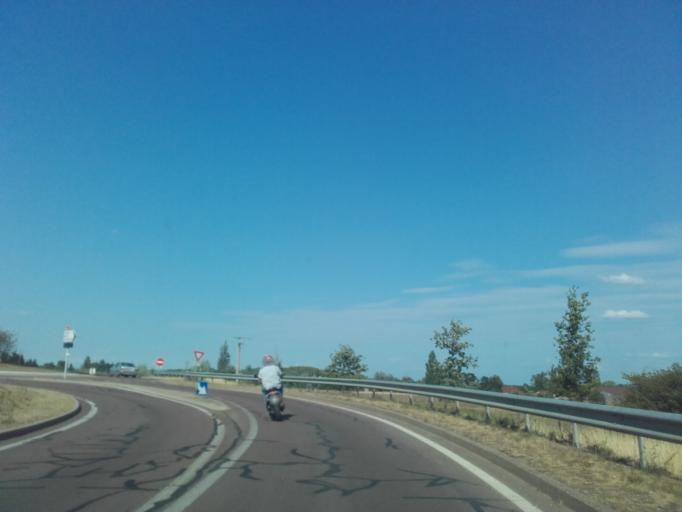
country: FR
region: Bourgogne
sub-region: Departement de Saone-et-Loire
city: Givry
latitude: 46.7557
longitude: 4.7213
